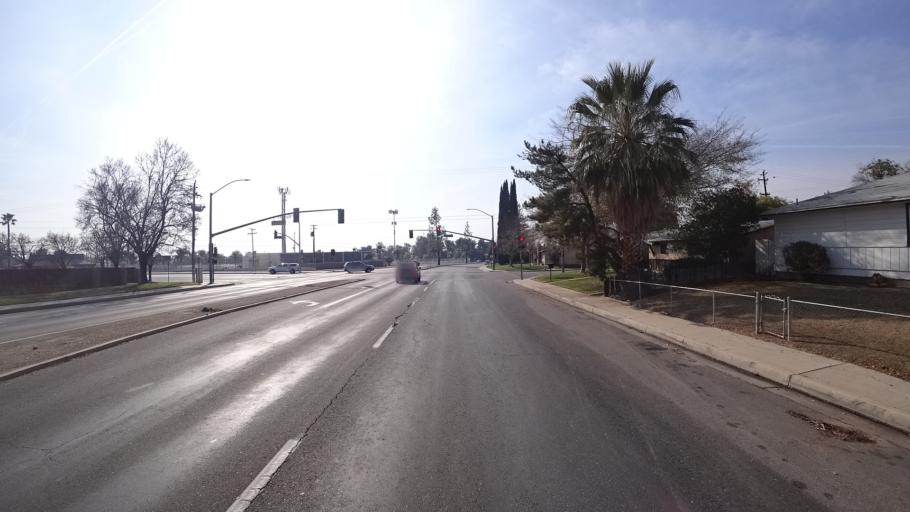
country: US
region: California
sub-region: Kern County
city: Oildale
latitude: 35.3990
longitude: -118.9528
